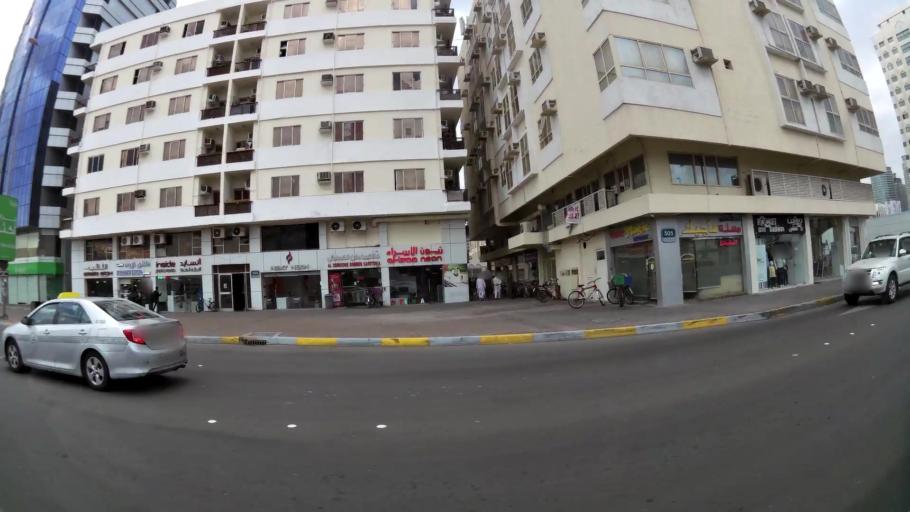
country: AE
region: Abu Dhabi
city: Abu Dhabi
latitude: 24.4752
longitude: 54.3664
